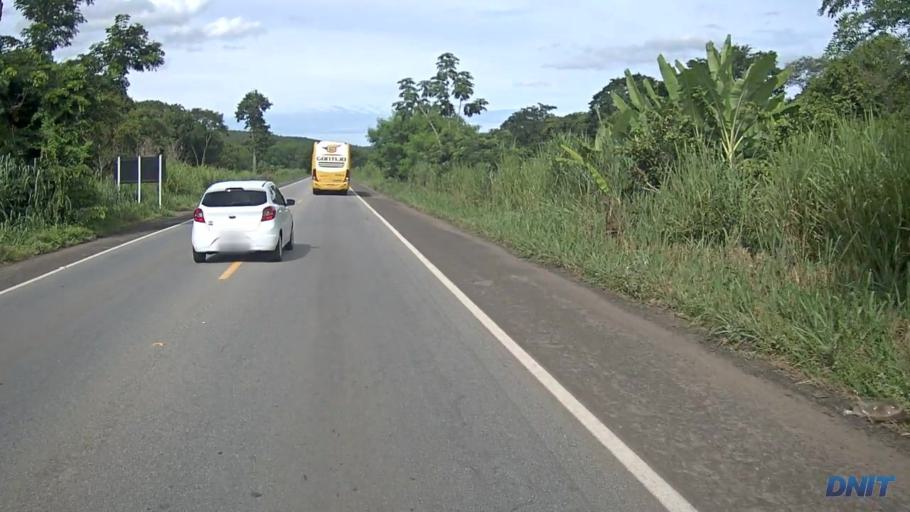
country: BR
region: Minas Gerais
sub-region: Ipaba
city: Ipaba
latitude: -19.2981
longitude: -42.3695
